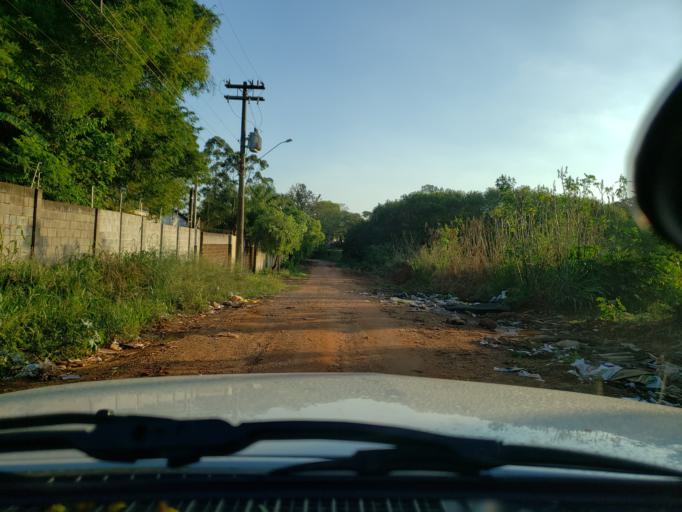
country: BR
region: Sao Paulo
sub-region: Moji-Guacu
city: Mogi-Gaucu
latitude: -22.3383
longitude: -46.9381
